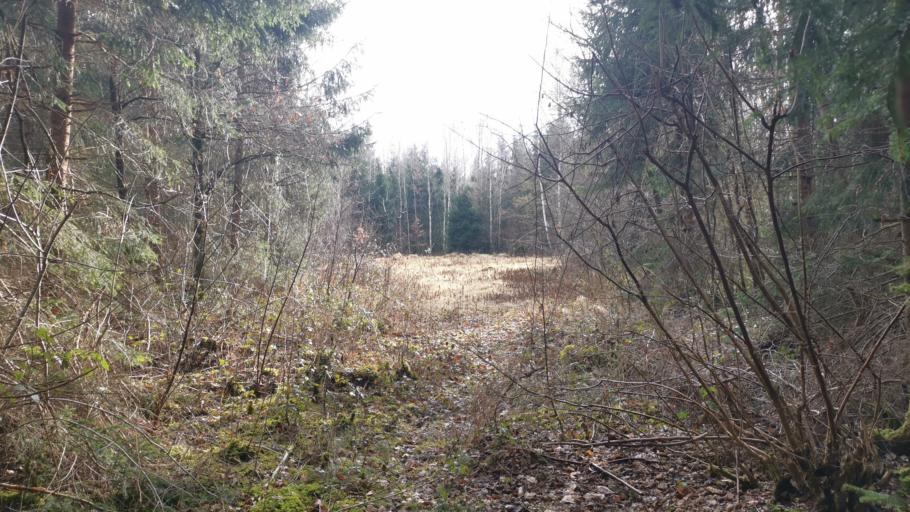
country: DE
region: Bavaria
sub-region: Upper Bavaria
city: Neuried
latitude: 48.0954
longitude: 11.4499
